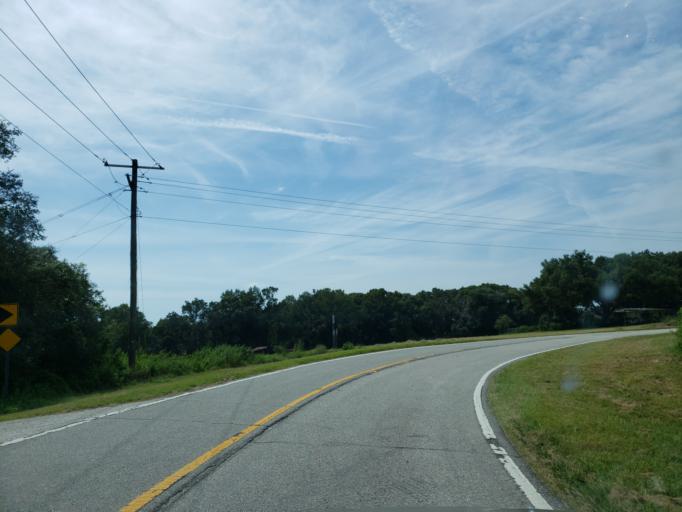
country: US
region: Florida
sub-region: Pasco County
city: San Antonio
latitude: 28.3724
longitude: -82.2783
